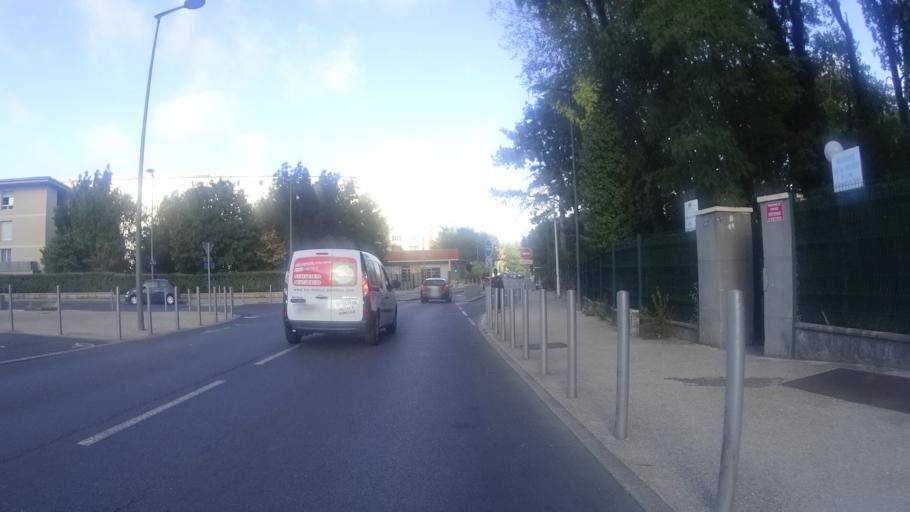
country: FR
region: Ile-de-France
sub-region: Departement de l'Essonne
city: Viry-Chatillon
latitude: 48.6807
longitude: 2.4007
